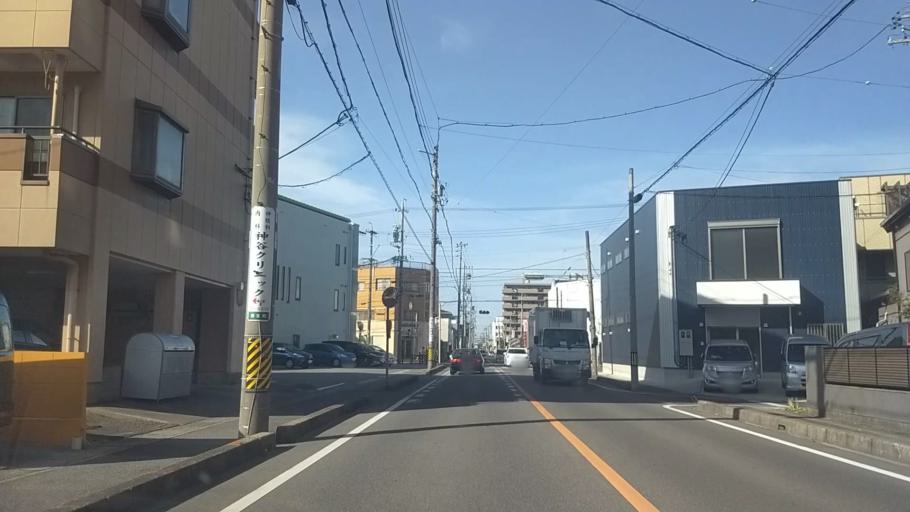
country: JP
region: Aichi
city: Anjo
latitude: 34.9549
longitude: 137.0894
